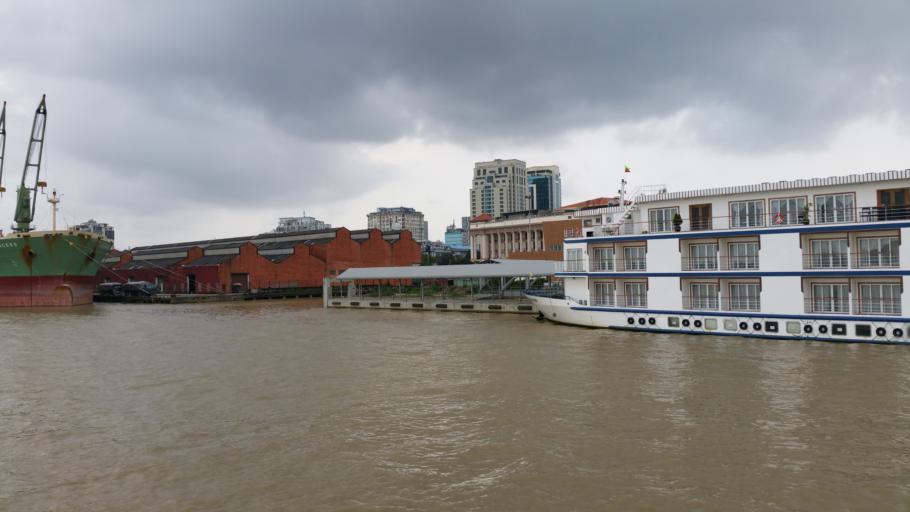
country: MM
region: Yangon
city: Yangon
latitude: 16.7676
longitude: 96.1605
